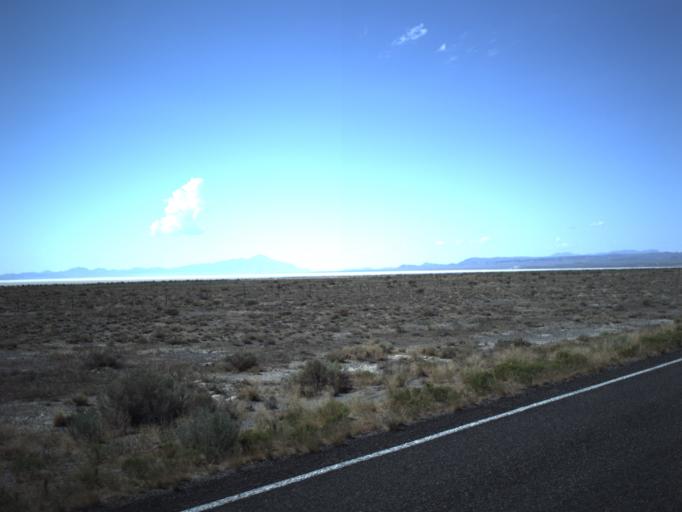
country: US
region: Utah
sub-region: Millard County
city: Delta
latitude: 39.1038
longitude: -113.1486
